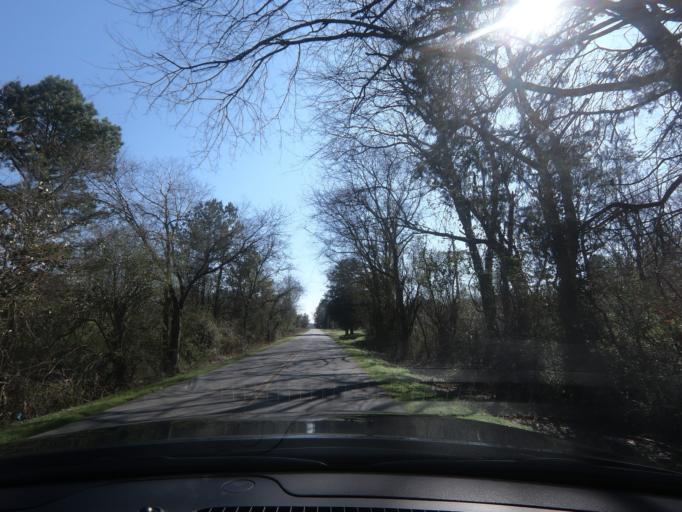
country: US
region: Georgia
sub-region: Bartow County
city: Rydal
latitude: 34.4368
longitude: -84.8065
